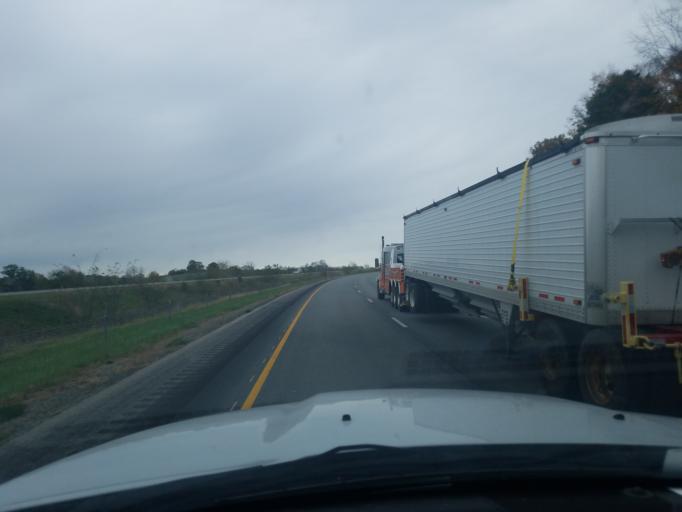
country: US
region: Indiana
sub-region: Dubois County
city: Ferdinand
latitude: 38.2326
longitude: -86.6746
